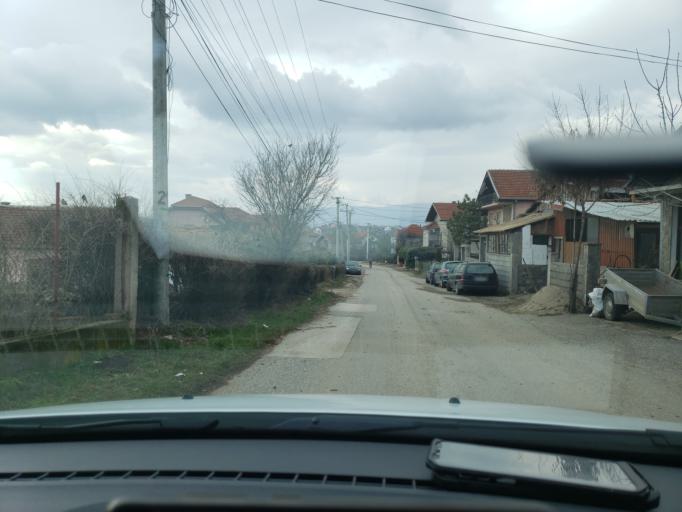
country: MK
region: Kumanovo
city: Kumanovo
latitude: 42.1462
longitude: 21.7439
